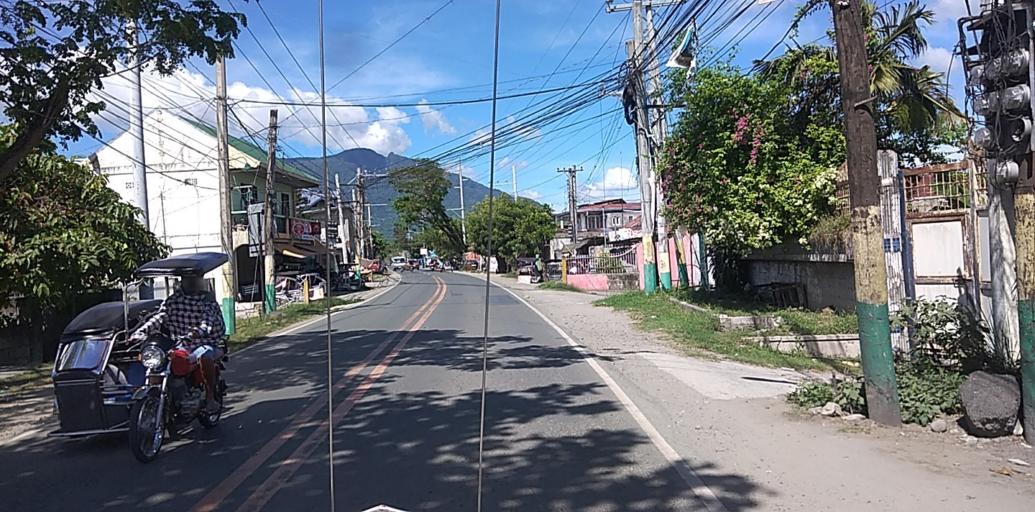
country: PH
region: Central Luzon
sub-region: Province of Pampanga
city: Arayat
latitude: 15.1402
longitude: 120.7728
